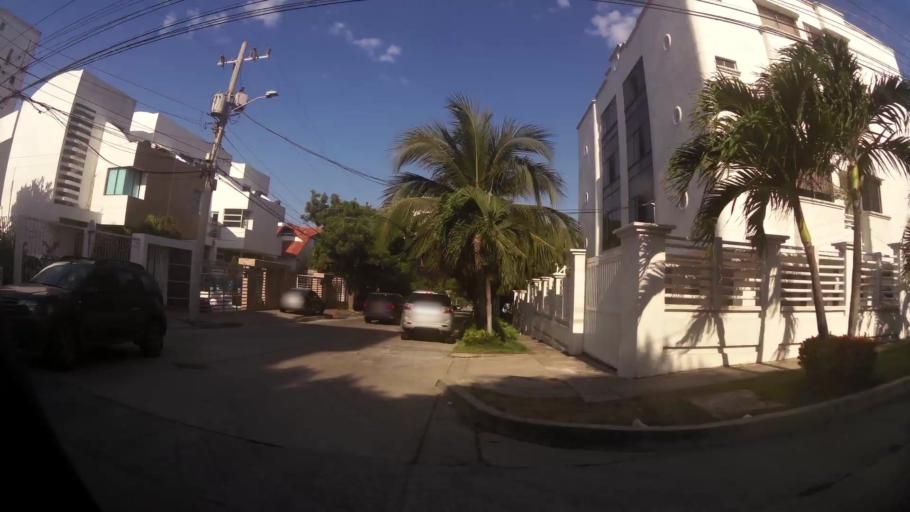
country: CO
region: Atlantico
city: Barranquilla
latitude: 11.0113
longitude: -74.8324
